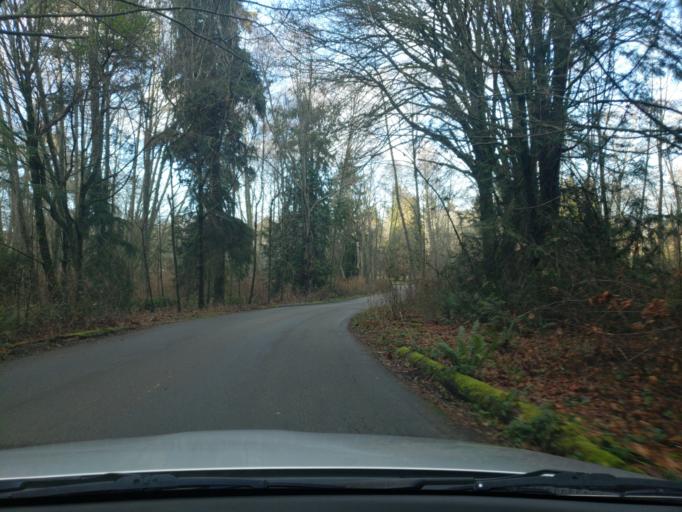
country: US
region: Washington
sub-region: King County
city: Seattle
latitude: 47.6631
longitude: -122.4110
